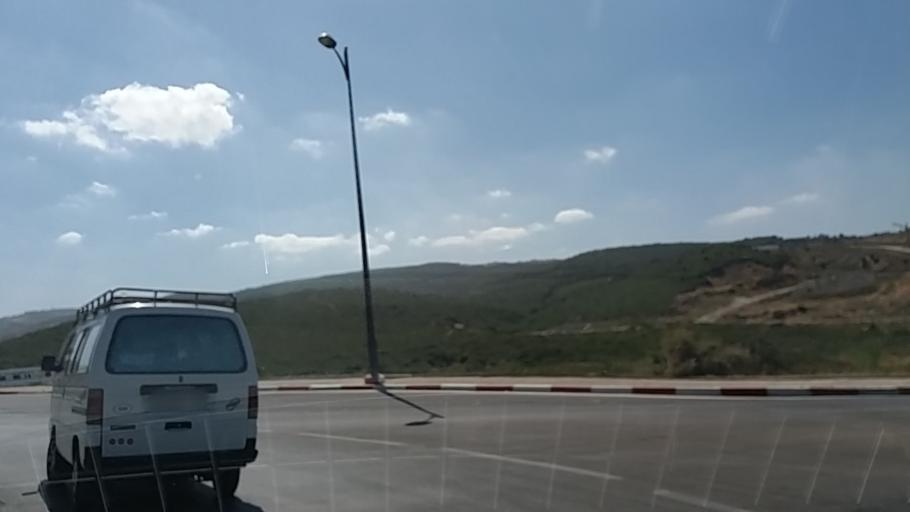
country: MA
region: Tanger-Tetouan
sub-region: Tanger-Assilah
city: Tangier
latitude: 35.7887
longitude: -5.7546
